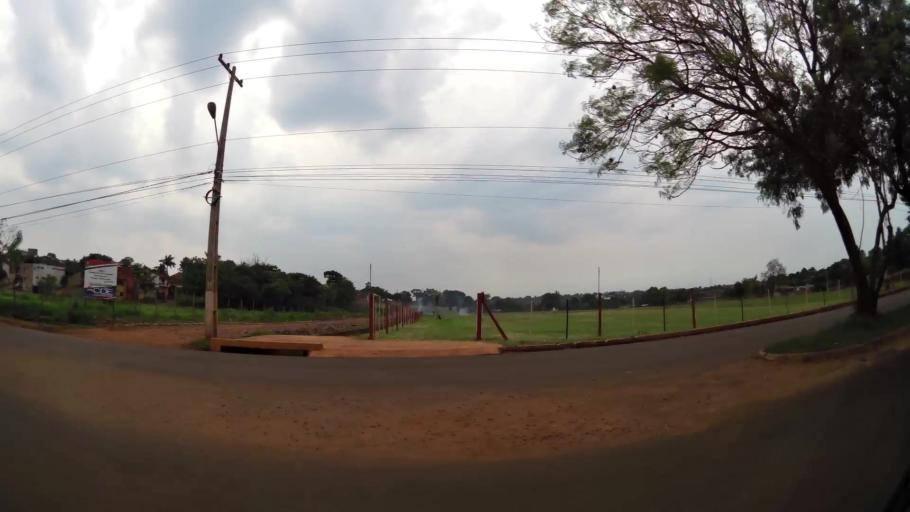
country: PY
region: Alto Parana
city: Presidente Franco
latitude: -25.5240
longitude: -54.6458
